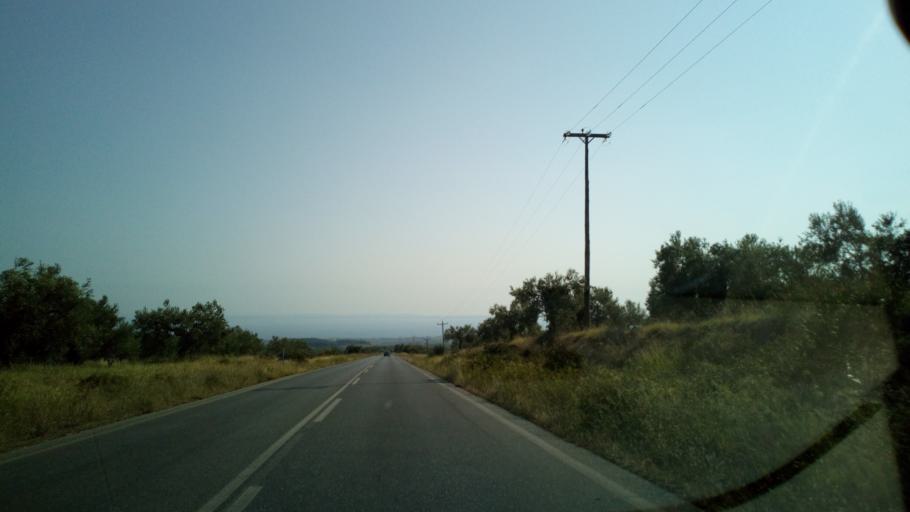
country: GR
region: Central Macedonia
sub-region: Nomos Chalkidikis
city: Polygyros
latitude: 40.3235
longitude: 23.4485
